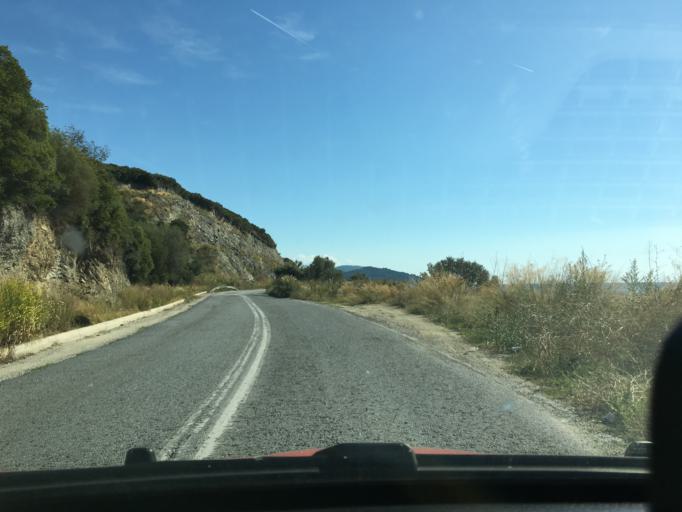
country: GR
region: Central Macedonia
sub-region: Nomos Chalkidikis
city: Nea Roda
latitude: 40.3565
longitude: 23.9433
